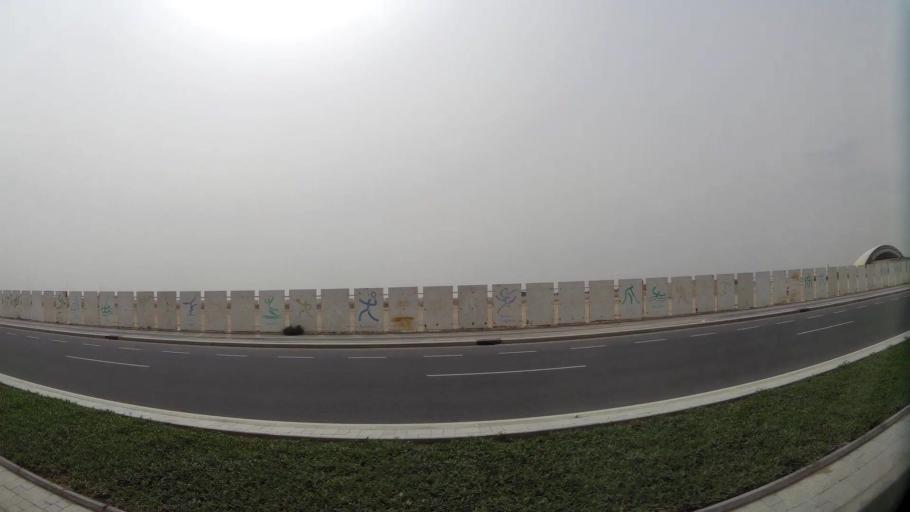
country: QA
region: Baladiyat ad Dawhah
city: Doha
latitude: 25.2259
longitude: 51.5360
